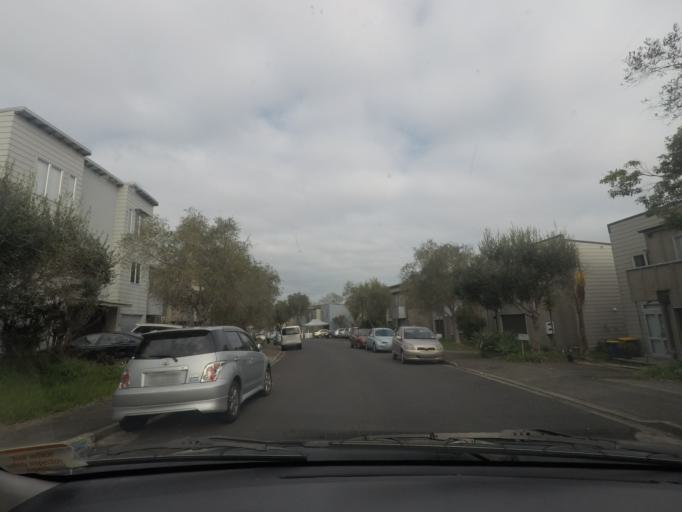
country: NZ
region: Auckland
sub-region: Auckland
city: Waitakere
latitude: -36.9071
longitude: 174.6325
